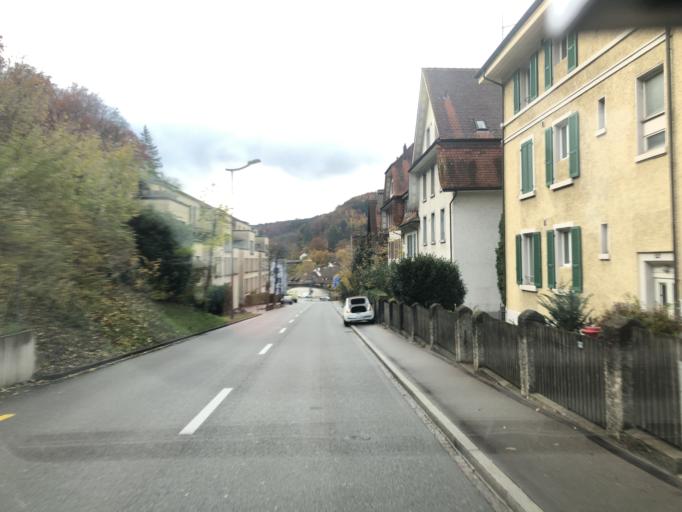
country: CH
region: Aargau
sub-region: Bezirk Baden
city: Wettingen
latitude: 47.4751
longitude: 8.3125
